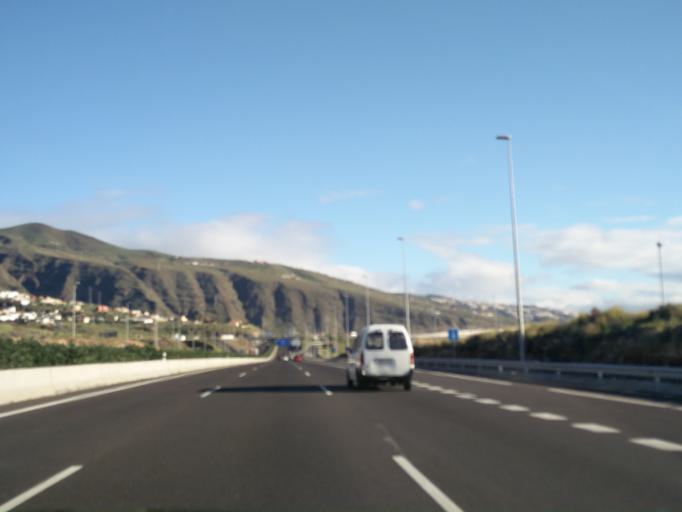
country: ES
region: Canary Islands
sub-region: Provincia de Santa Cruz de Tenerife
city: Candelaria
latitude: 28.3650
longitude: -16.3697
